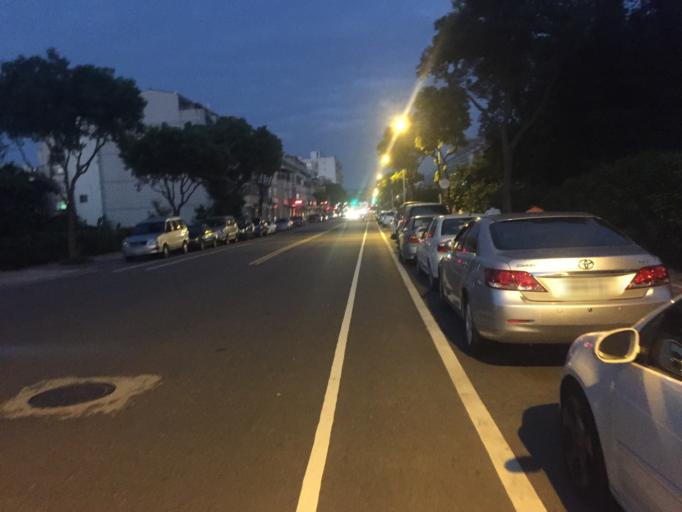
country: TW
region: Taiwan
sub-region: Taoyuan
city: Taoyuan
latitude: 24.9778
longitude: 121.3171
